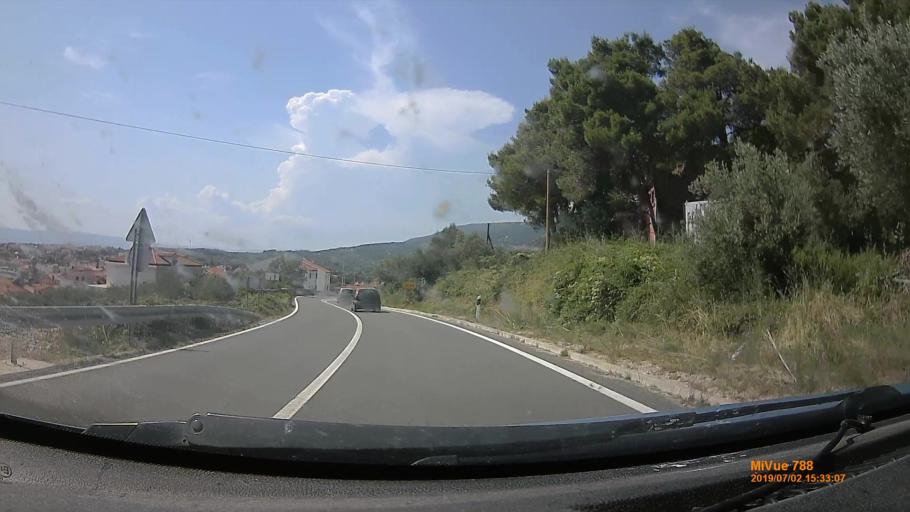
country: HR
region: Primorsko-Goranska
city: Cres
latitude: 44.9572
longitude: 14.4166
